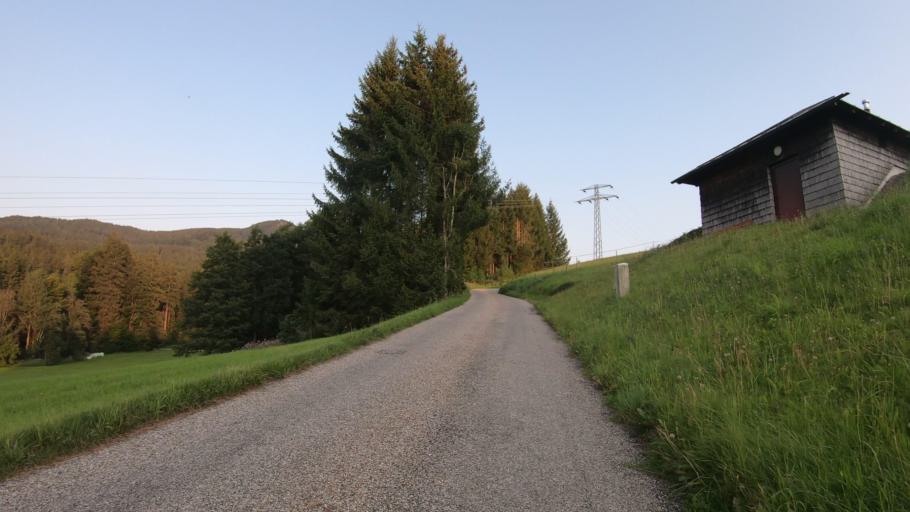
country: DE
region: Bavaria
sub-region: Upper Bavaria
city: Ruhpolding
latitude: 47.7889
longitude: 12.6462
